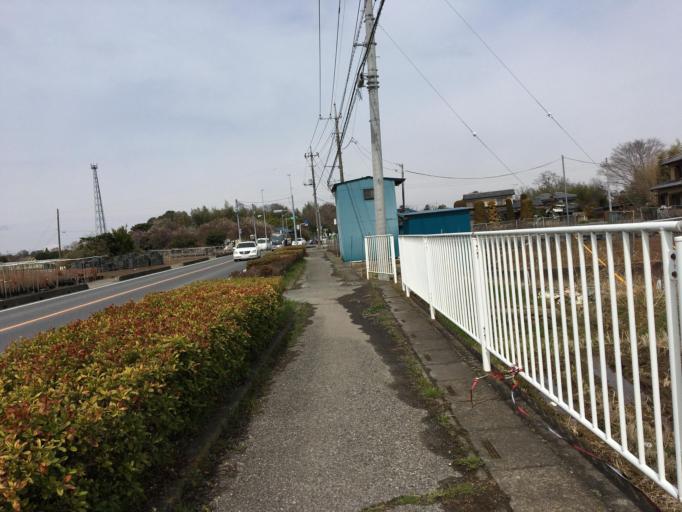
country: JP
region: Saitama
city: Yorii
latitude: 36.1433
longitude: 139.2096
